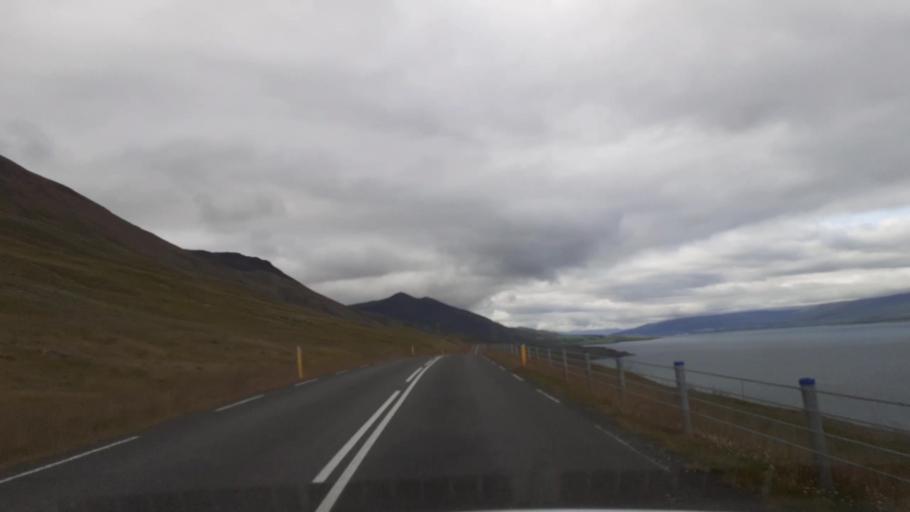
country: IS
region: Northeast
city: Akureyri
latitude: 65.8562
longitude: -18.0621
